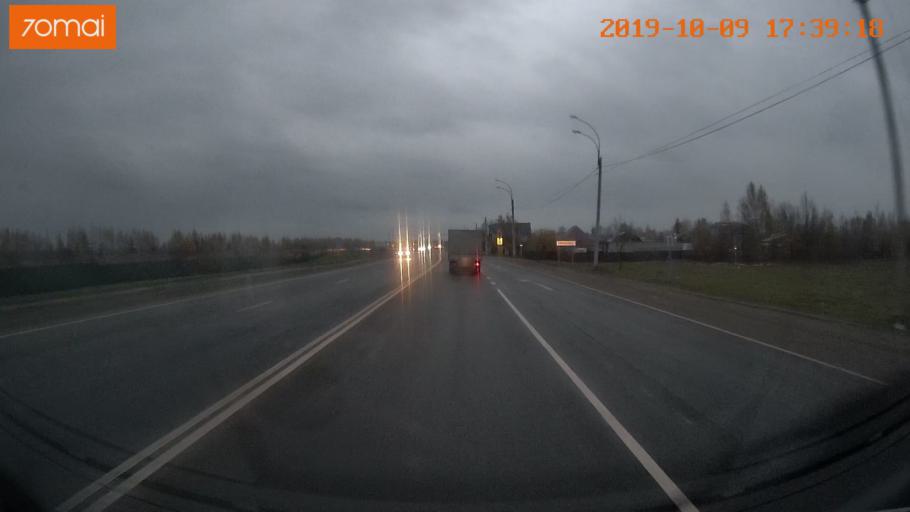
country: RU
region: Ivanovo
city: Bogorodskoye
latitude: 57.0618
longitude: 40.9568
